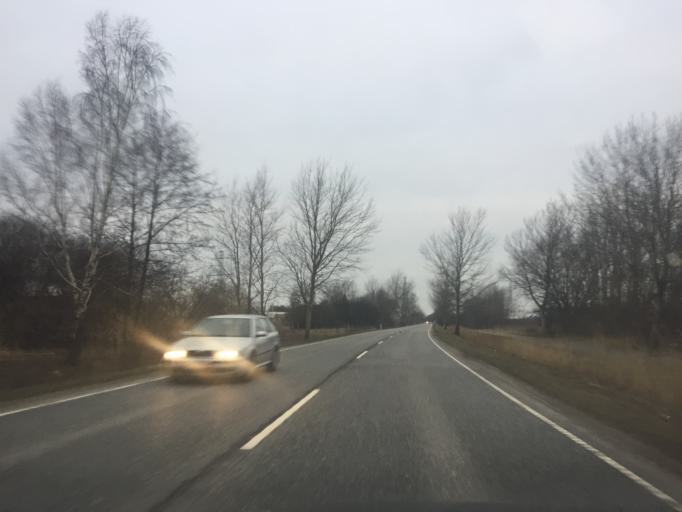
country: DK
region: Capital Region
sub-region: Frederikssund Kommune
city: Slangerup
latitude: 55.8394
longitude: 12.1603
